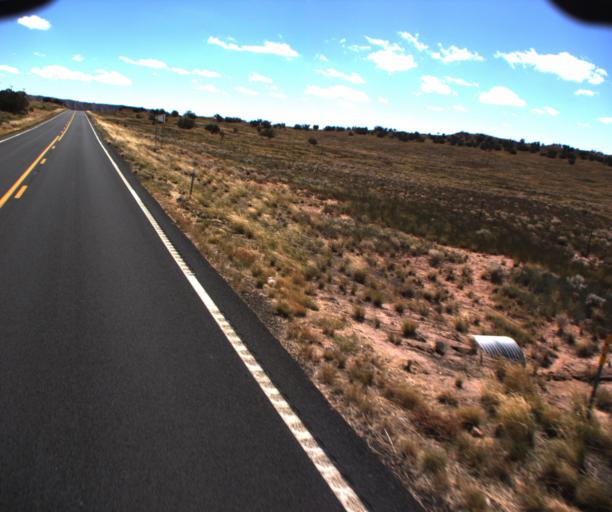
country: US
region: Arizona
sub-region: Apache County
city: Houck
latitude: 35.0728
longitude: -109.2913
